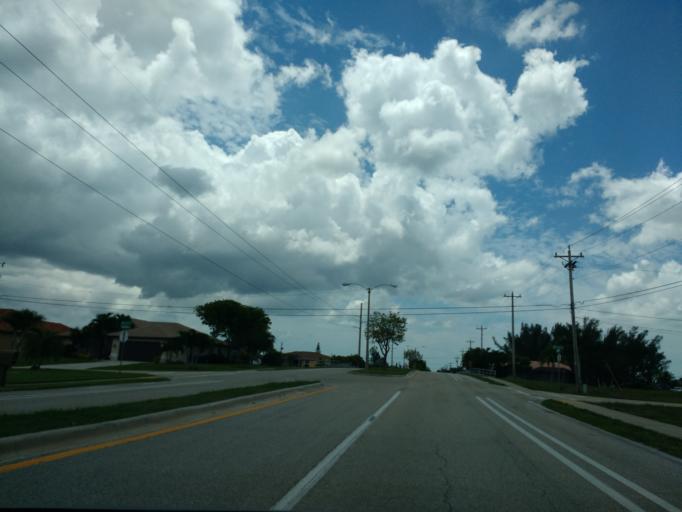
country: US
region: Florida
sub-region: Lee County
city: Cape Coral
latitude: 26.5688
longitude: -82.0174
